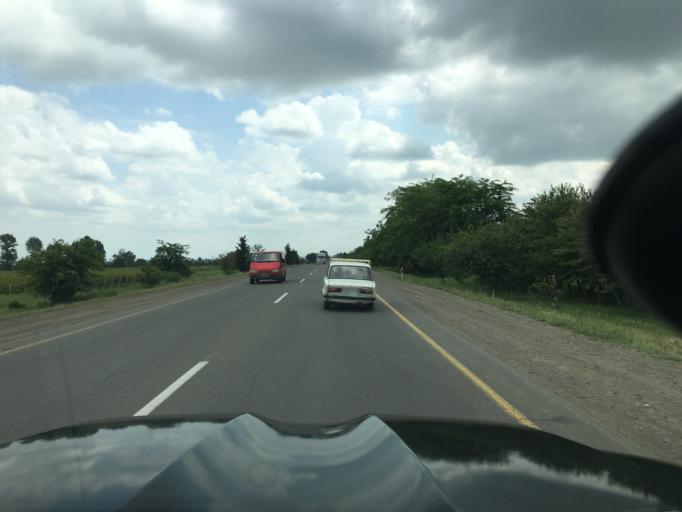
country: AZ
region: Tovuz
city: Tovuz
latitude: 40.9673
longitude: 45.6998
